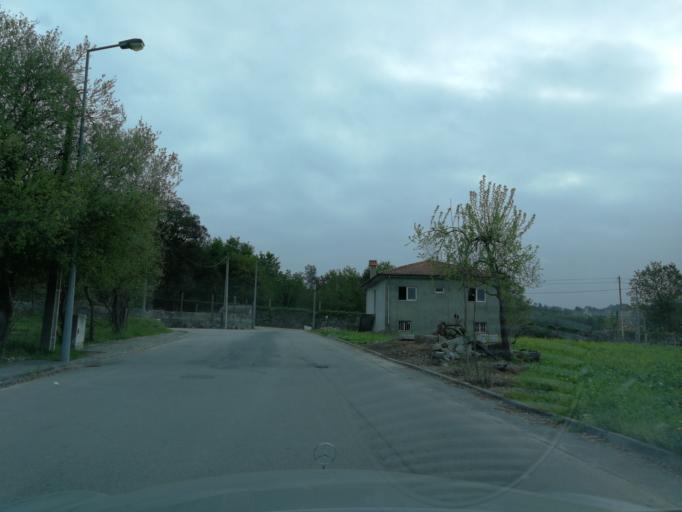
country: PT
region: Braga
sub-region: Braga
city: Braga
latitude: 41.5793
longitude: -8.4405
